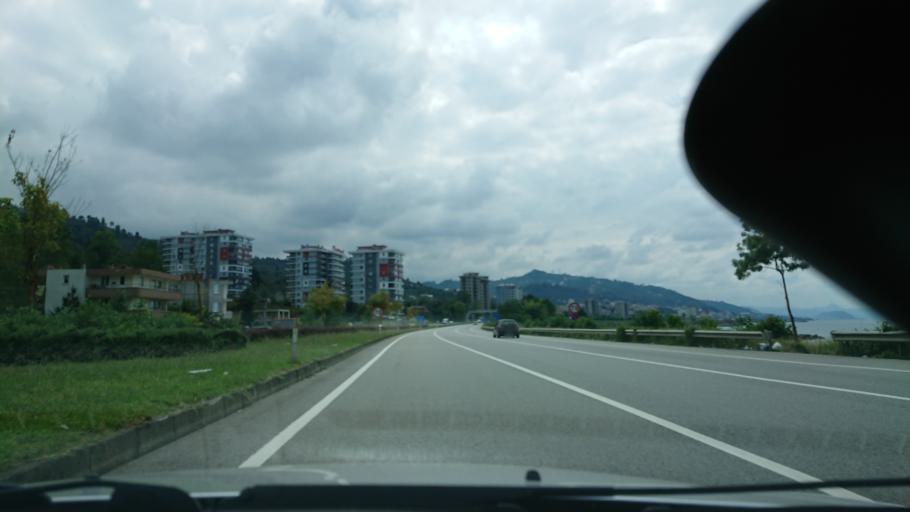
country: TR
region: Giresun
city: Kesap
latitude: 40.9193
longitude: 38.5379
